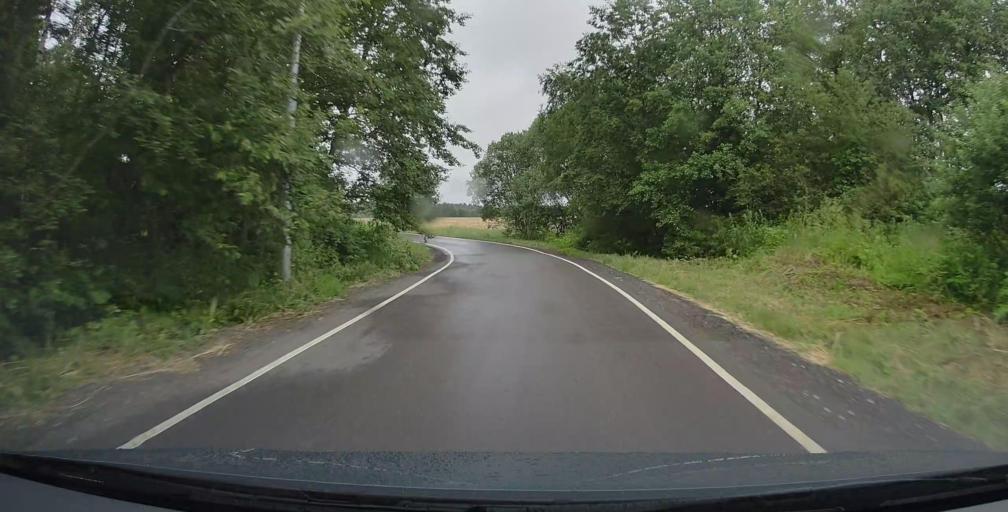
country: RU
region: Moskovskaya
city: Selyatino
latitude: 55.4034
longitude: 37.0179
